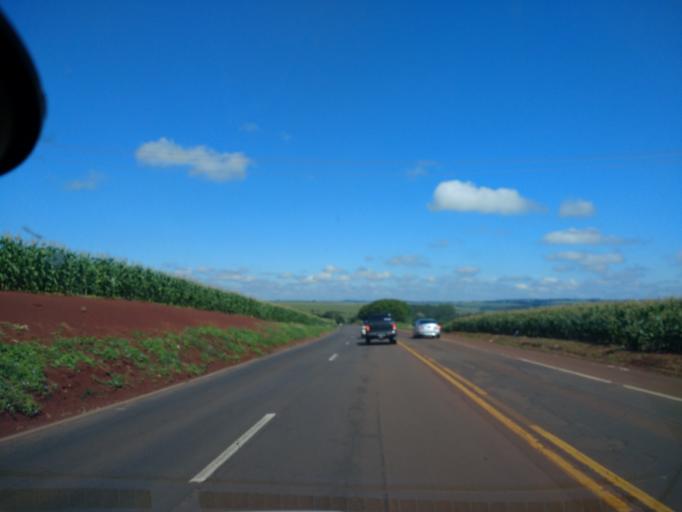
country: BR
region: Parana
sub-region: Cianorte
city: Cianorte
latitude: -23.6464
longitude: -52.4856
